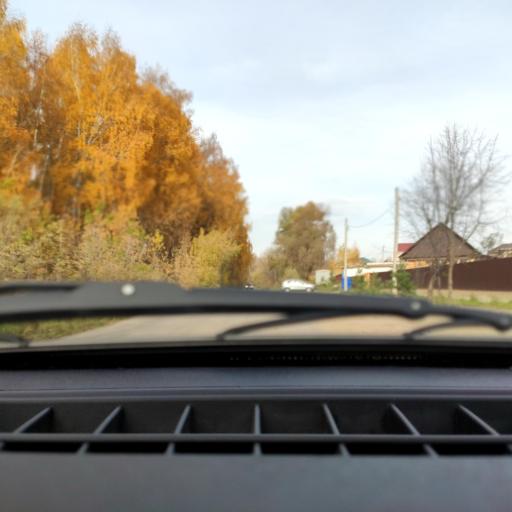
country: RU
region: Bashkortostan
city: Ufa
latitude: 54.7884
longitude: 56.1593
